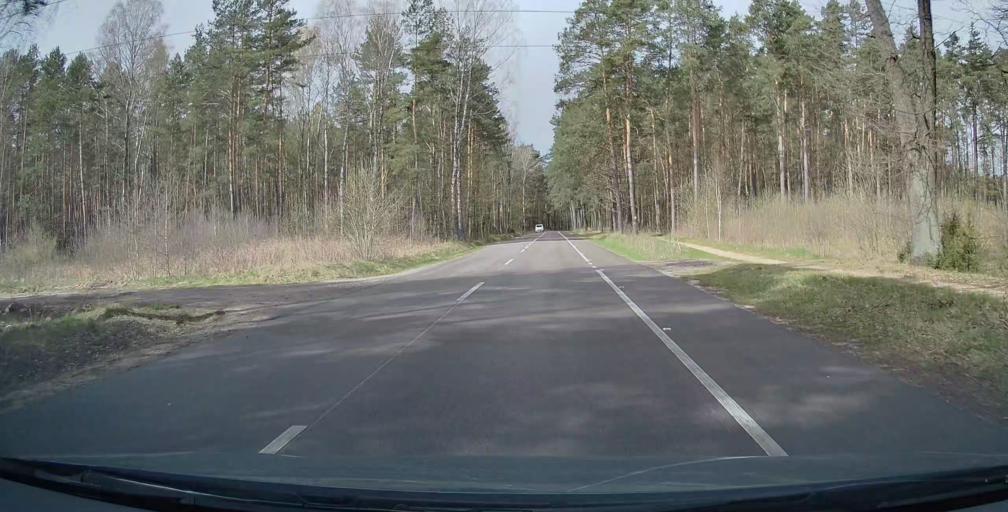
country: PL
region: Masovian Voivodeship
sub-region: Powiat wyszkowski
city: Dlugosiodlo
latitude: 52.7612
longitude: 21.5772
